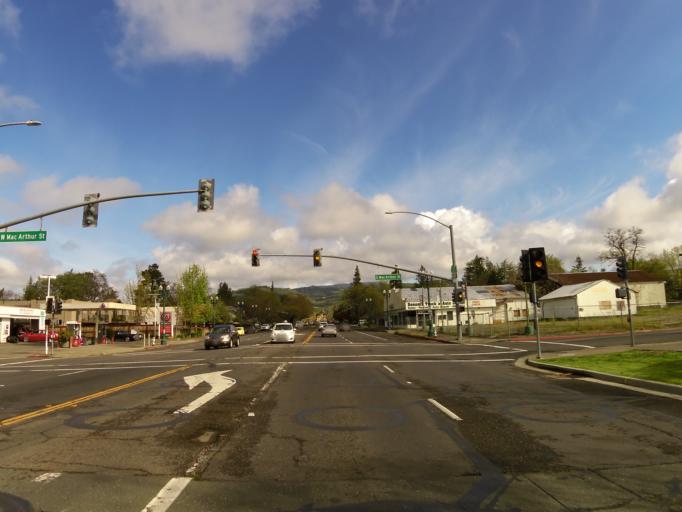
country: US
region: California
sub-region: Sonoma County
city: Sonoma
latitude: 38.2845
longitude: -122.4590
